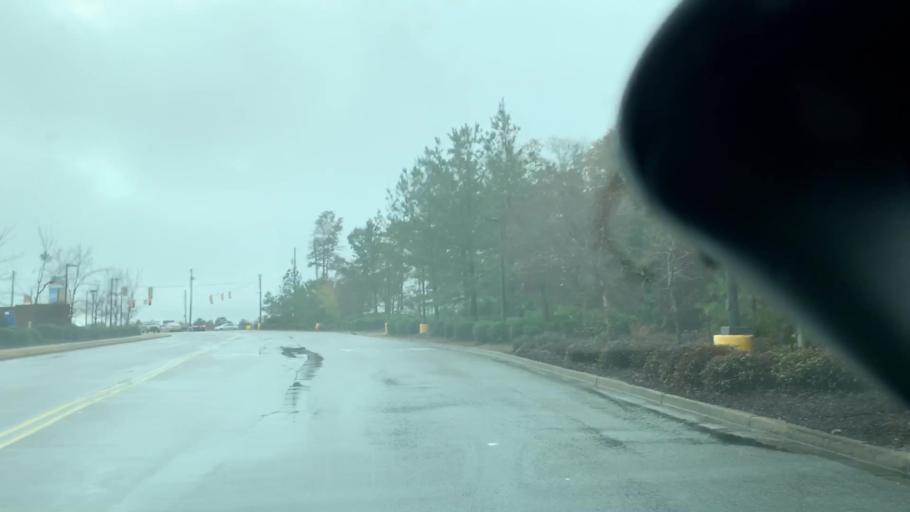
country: US
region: South Carolina
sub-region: Richland County
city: Dentsville
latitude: 34.1350
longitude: -80.9684
